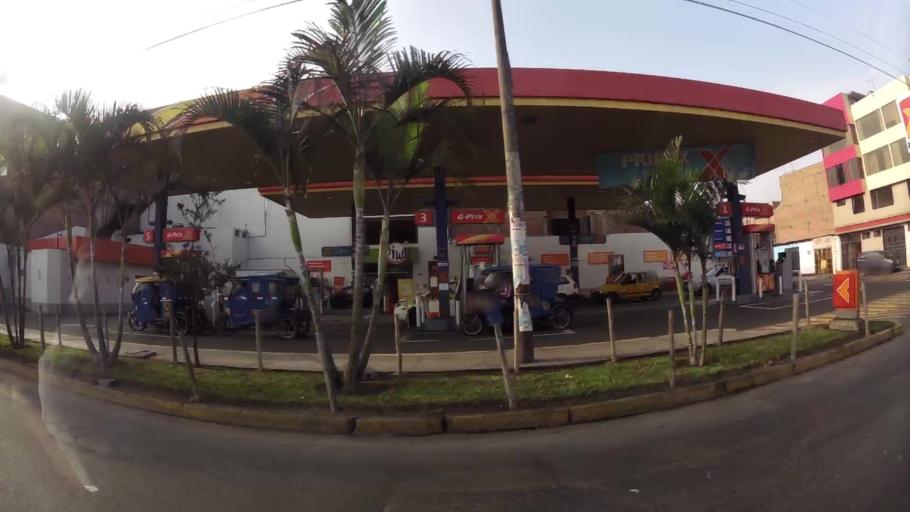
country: PE
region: Lima
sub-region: Lima
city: Independencia
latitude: -12.0243
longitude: -77.0797
